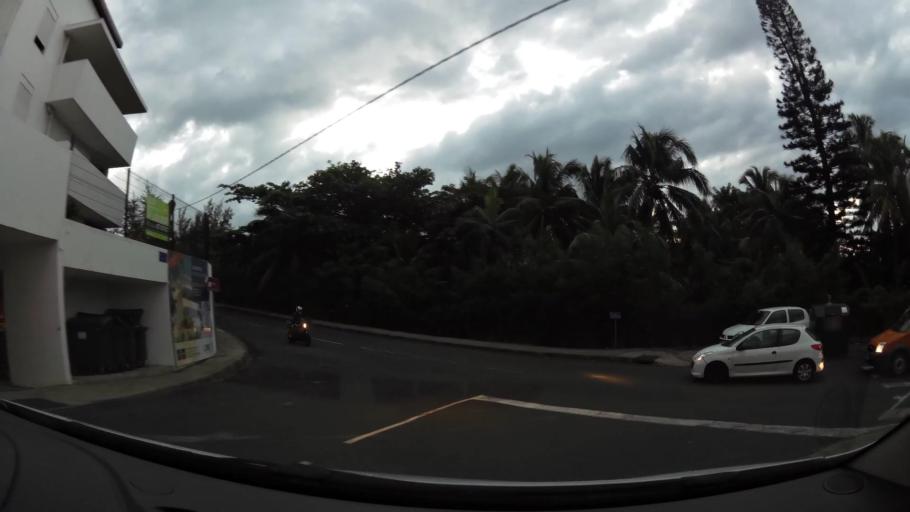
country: RE
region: Reunion
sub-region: Reunion
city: Saint-Denis
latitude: -20.9004
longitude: 55.4663
